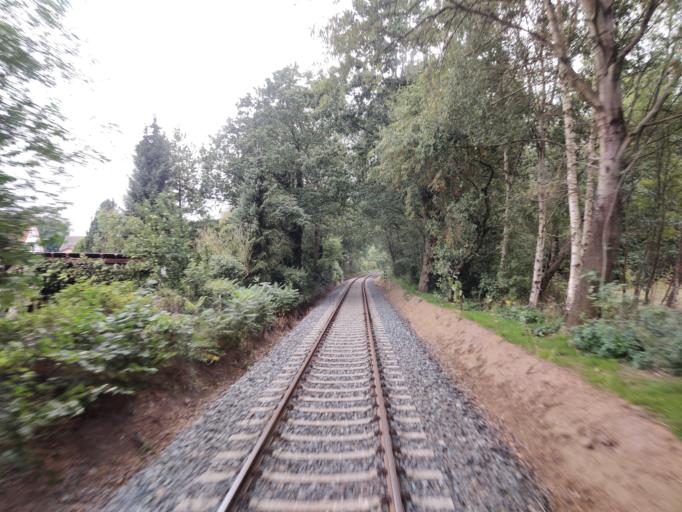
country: DE
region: Lower Saxony
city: Worpswede
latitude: 53.2683
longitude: 8.9603
